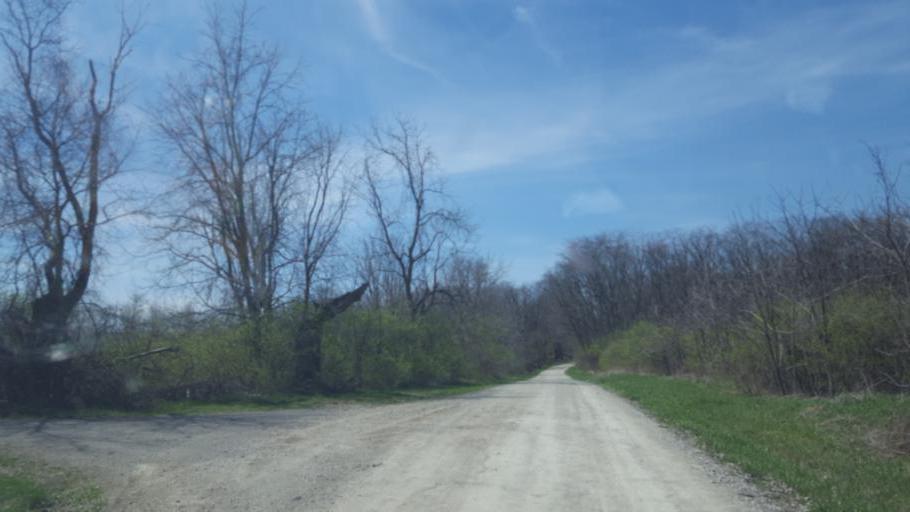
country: US
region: Ohio
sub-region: Delaware County
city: Ashley
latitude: 40.4092
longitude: -83.0349
